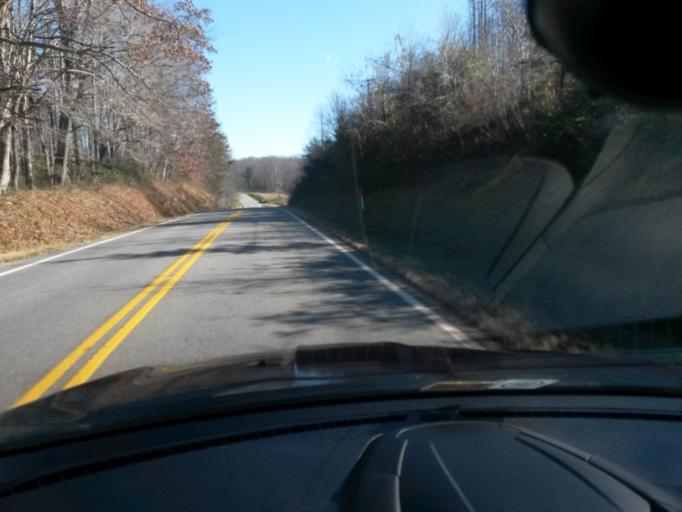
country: US
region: Virginia
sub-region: Patrick County
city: Patrick Springs
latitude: 36.7678
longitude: -80.1597
